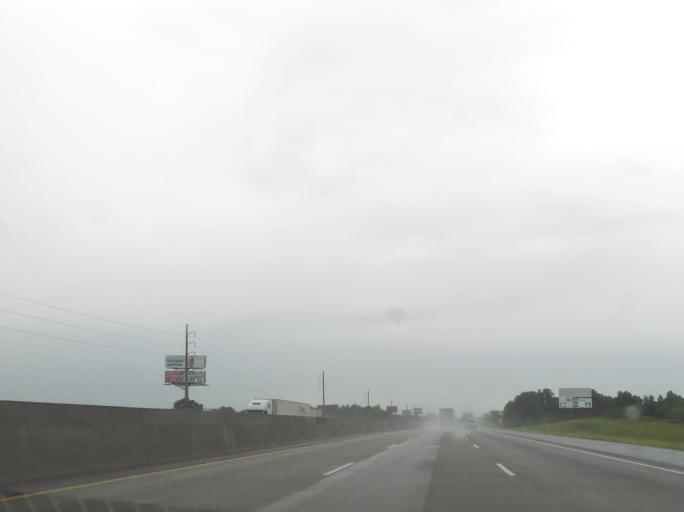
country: US
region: Georgia
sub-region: Tift County
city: Unionville
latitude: 31.4106
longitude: -83.5035
